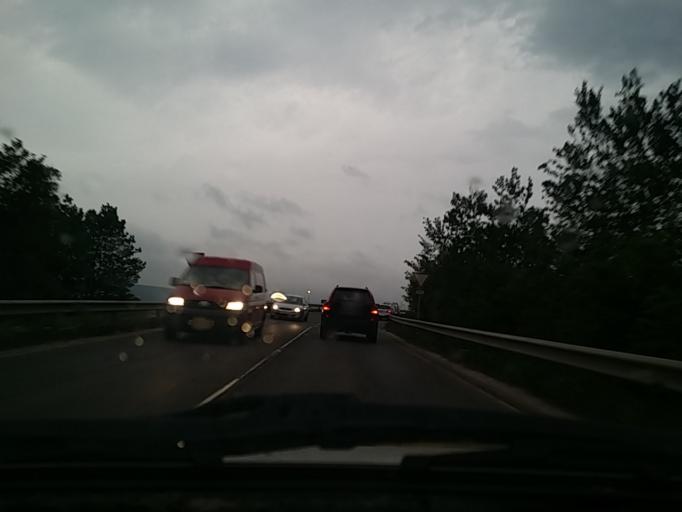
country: HU
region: Pest
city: Pilisborosjeno
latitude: 47.5968
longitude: 18.9679
